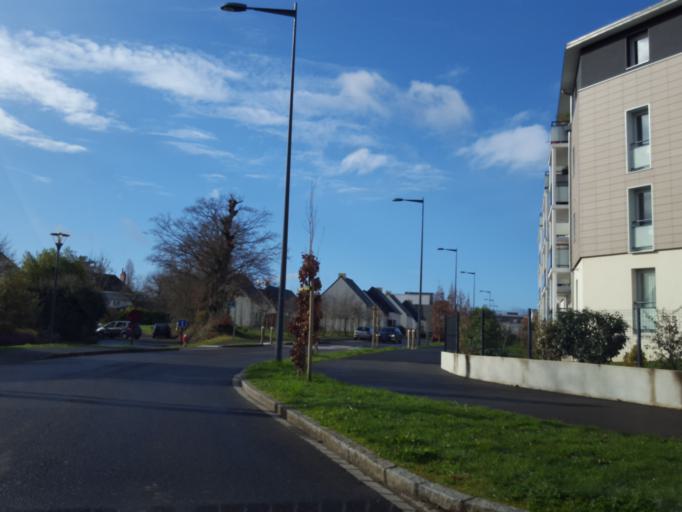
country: FR
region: Brittany
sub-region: Departement d'Ille-et-Vilaine
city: Bruz
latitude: 48.0282
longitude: -1.7531
